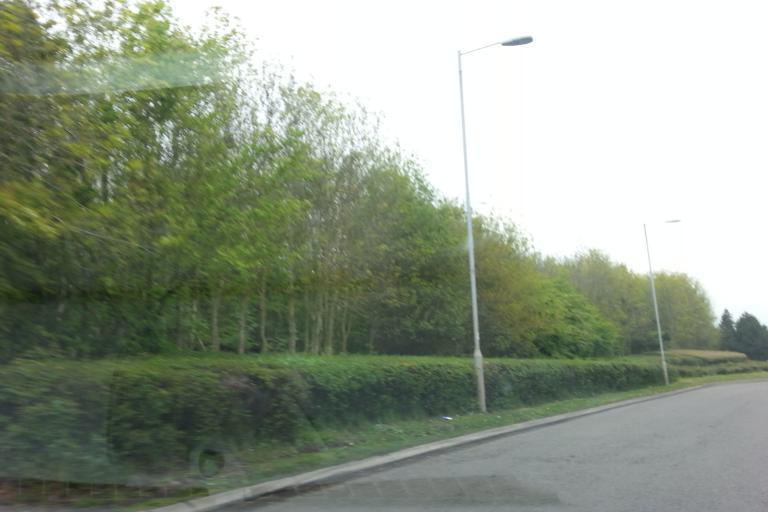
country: GB
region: England
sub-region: Leicestershire
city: Kegworth
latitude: 52.8235
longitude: -1.3084
